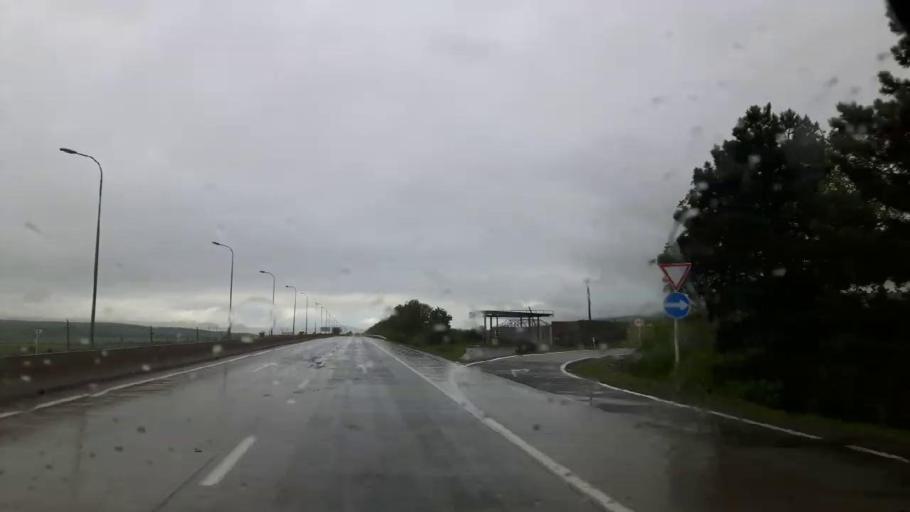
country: GE
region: Shida Kartli
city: Kaspi
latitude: 42.0212
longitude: 44.2955
